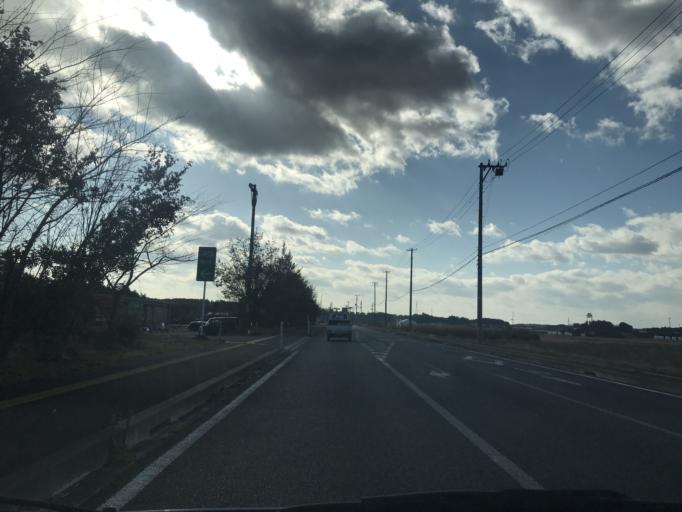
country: JP
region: Iwate
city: Ichinoseki
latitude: 38.7494
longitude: 141.0665
